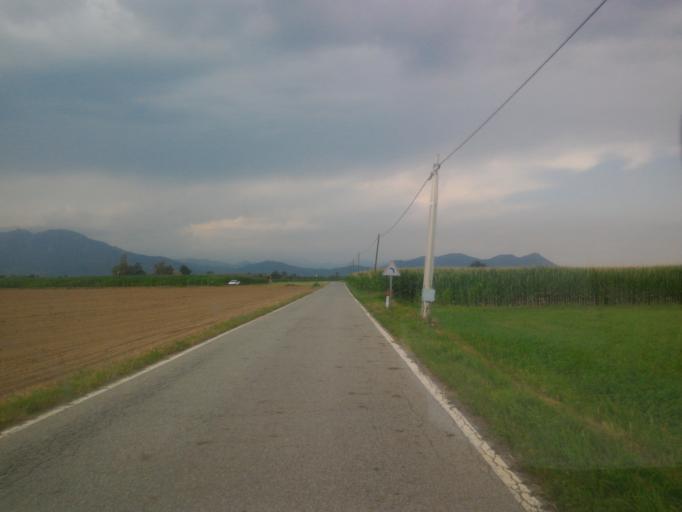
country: IT
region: Piedmont
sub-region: Provincia di Torino
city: Buriasco
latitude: 44.8827
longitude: 7.4020
